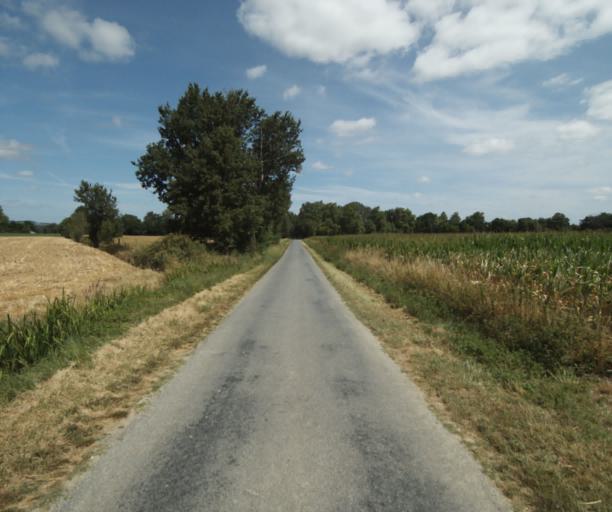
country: FR
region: Midi-Pyrenees
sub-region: Departement du Tarn
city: Soreze
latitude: 43.4904
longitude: 2.0792
